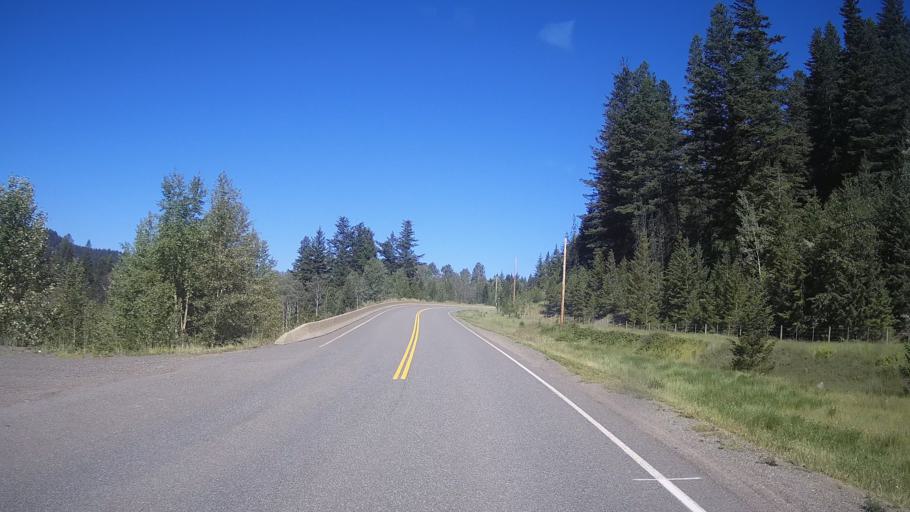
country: CA
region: British Columbia
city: Kamloops
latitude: 51.4764
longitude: -120.5582
